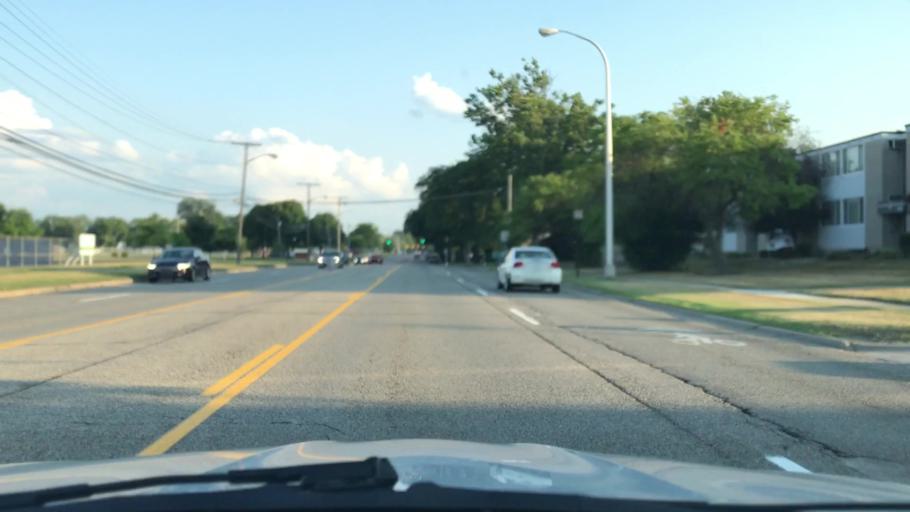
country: US
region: Michigan
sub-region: Oakland County
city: Clawson
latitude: 42.5233
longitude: -83.1651
